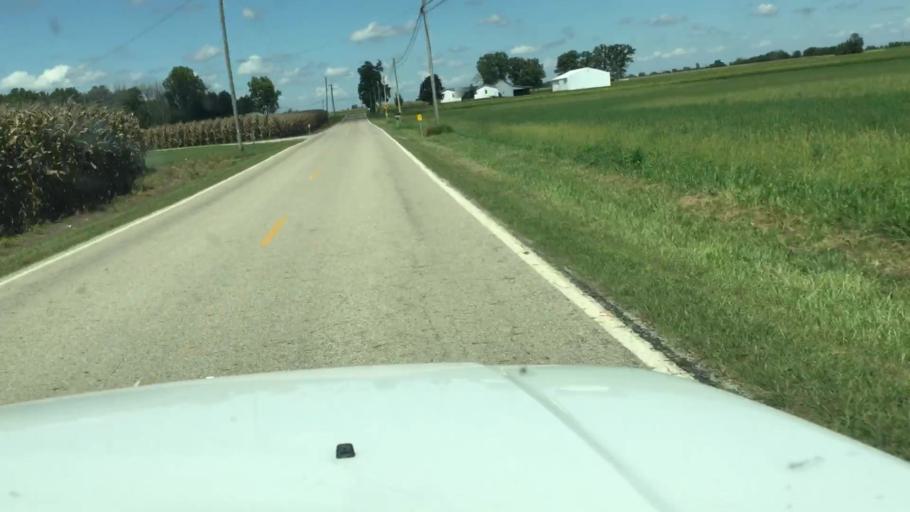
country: US
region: Ohio
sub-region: Madison County
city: Mount Sterling
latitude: 39.6874
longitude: -83.2364
